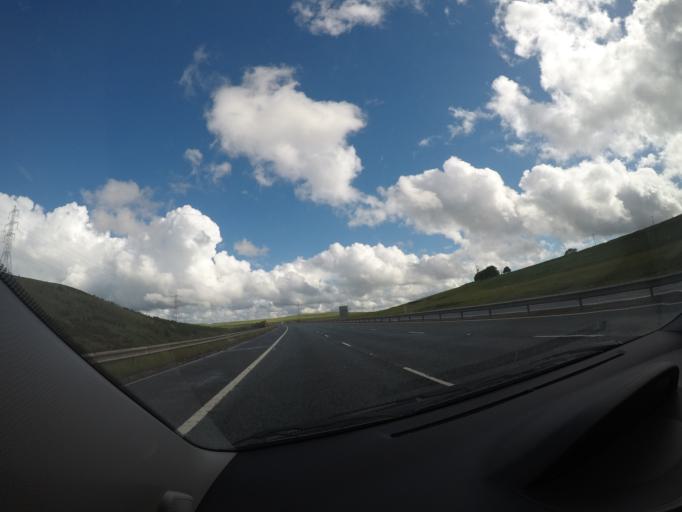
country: GB
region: Scotland
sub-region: South Lanarkshire
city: Douglas
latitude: 55.5495
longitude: -3.7997
